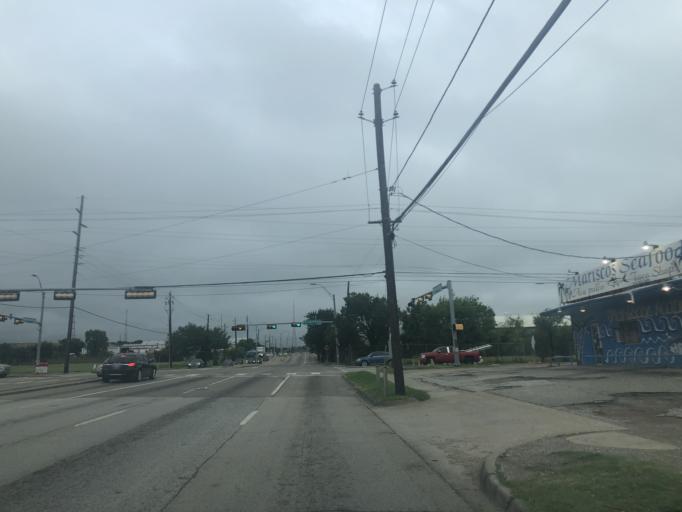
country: US
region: Texas
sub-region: Dallas County
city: Cockrell Hill
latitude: 32.7793
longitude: -96.8739
